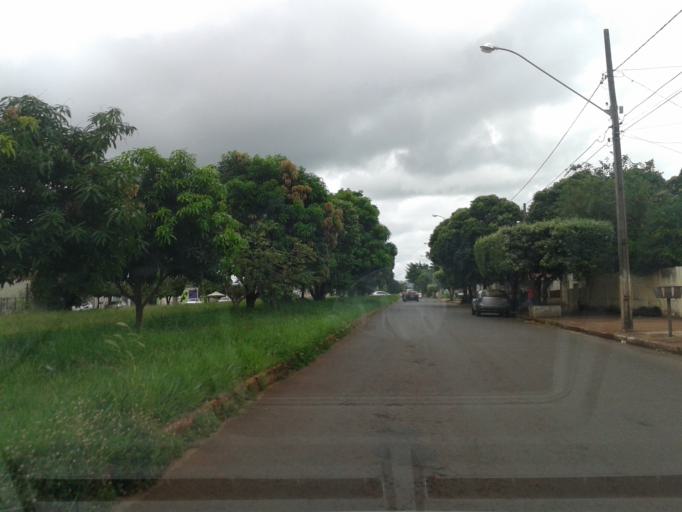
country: BR
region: Minas Gerais
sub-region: Ituiutaba
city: Ituiutaba
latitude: -18.9879
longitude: -49.4600
